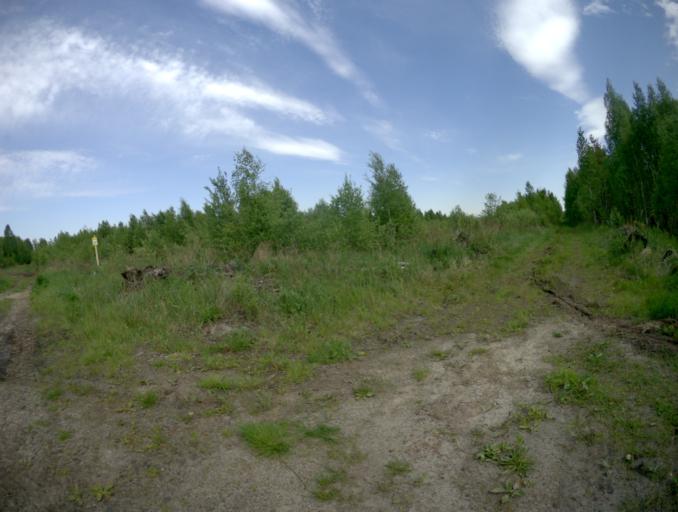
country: RU
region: Vladimir
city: Ivanishchi
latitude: 55.6960
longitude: 40.4716
